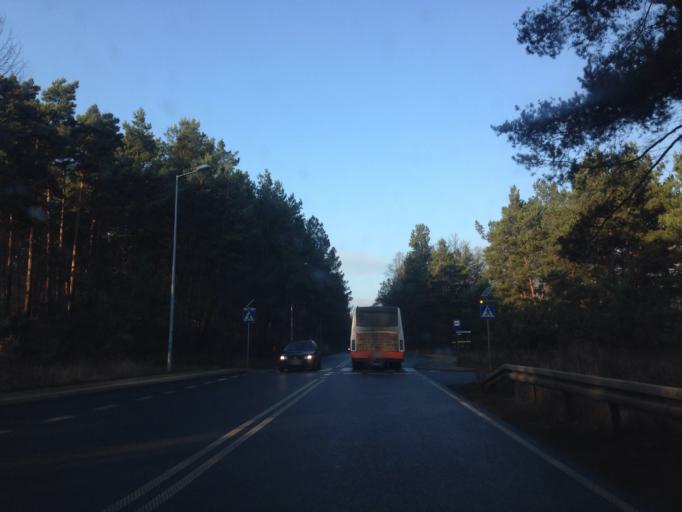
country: PL
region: Kujawsko-Pomorskie
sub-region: Bydgoszcz
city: Fordon
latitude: 53.0876
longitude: 18.1164
